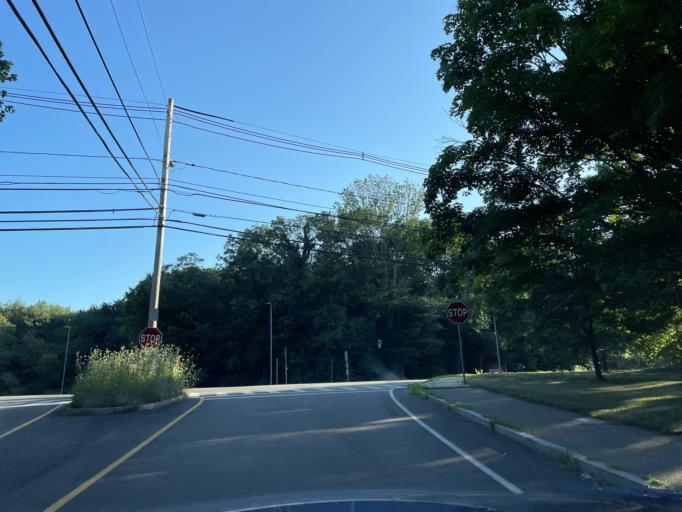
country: US
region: Massachusetts
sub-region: Plymouth County
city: Bridgewater
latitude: 41.9931
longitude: -70.9559
